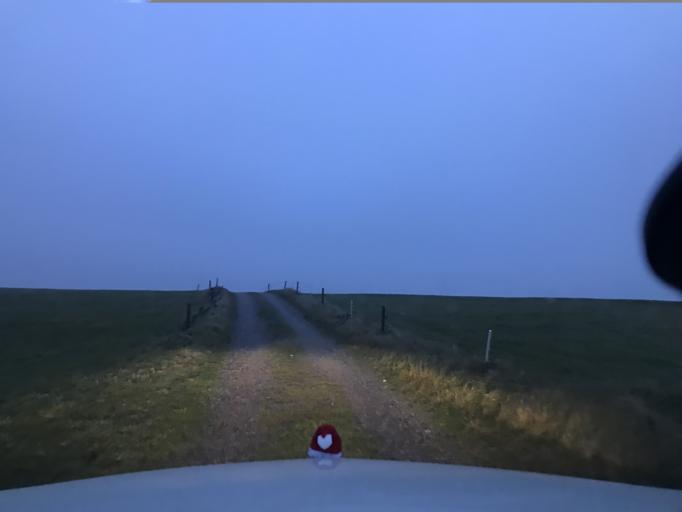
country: DK
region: South Denmark
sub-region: Esbjerg Kommune
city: Tjaereborg
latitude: 55.2659
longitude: 8.5469
